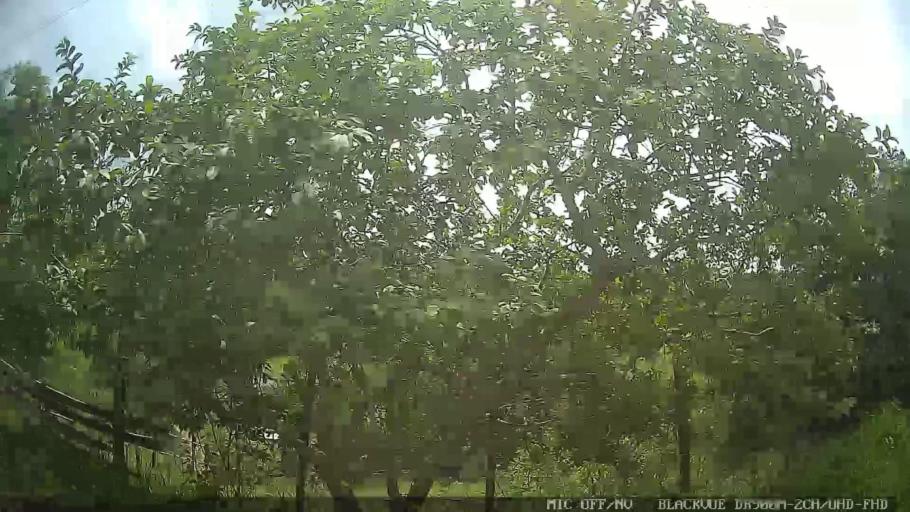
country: BR
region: Sao Paulo
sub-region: Santa Isabel
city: Santa Isabel
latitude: -23.3847
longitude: -46.2355
